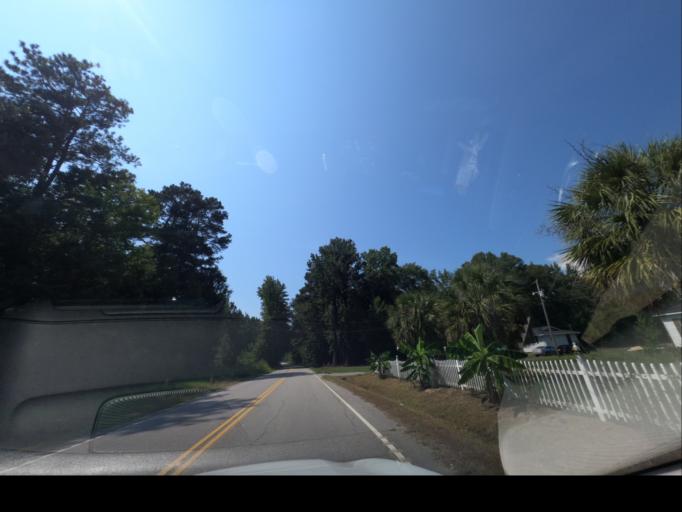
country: US
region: South Carolina
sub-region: Richland County
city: Hopkins
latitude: 33.8634
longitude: -80.8838
